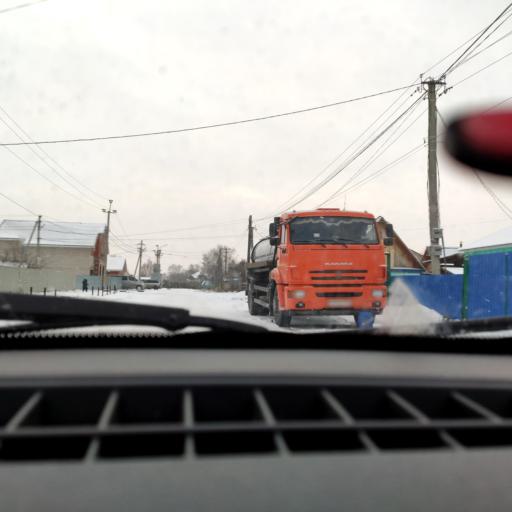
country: RU
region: Bashkortostan
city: Ufa
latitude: 54.6194
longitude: 55.9110
